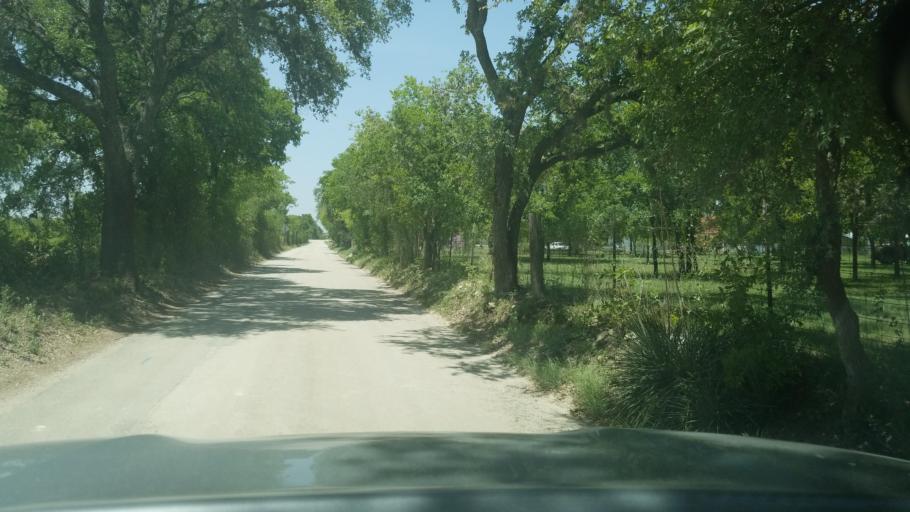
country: US
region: Texas
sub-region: Guadalupe County
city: Cibolo
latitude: 29.5851
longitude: -98.2326
